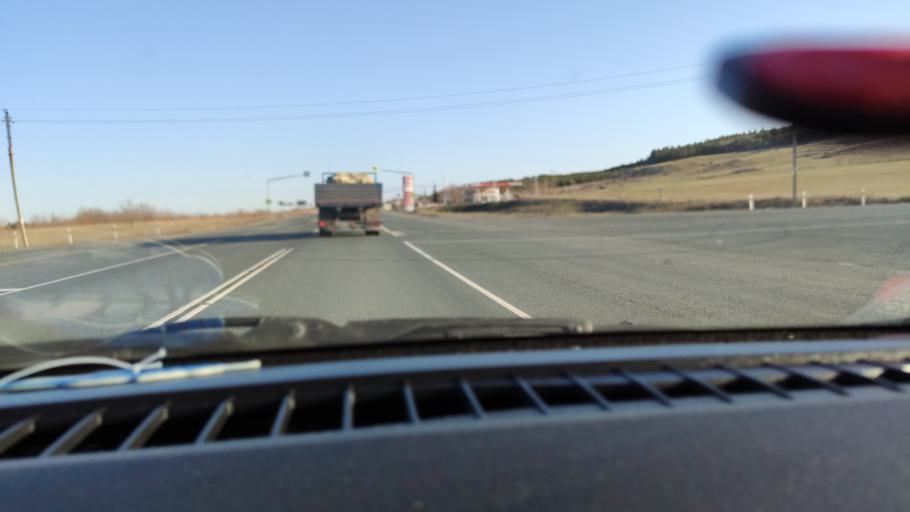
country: RU
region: Saratov
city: Alekseyevka
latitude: 52.2945
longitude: 47.9286
